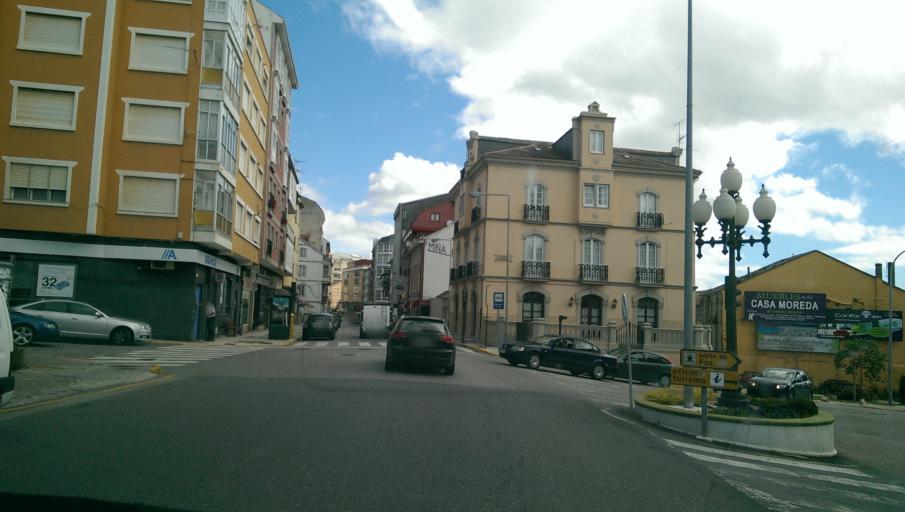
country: ES
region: Galicia
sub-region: Provincia de Lugo
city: Foz
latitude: 43.5659
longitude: -7.2605
